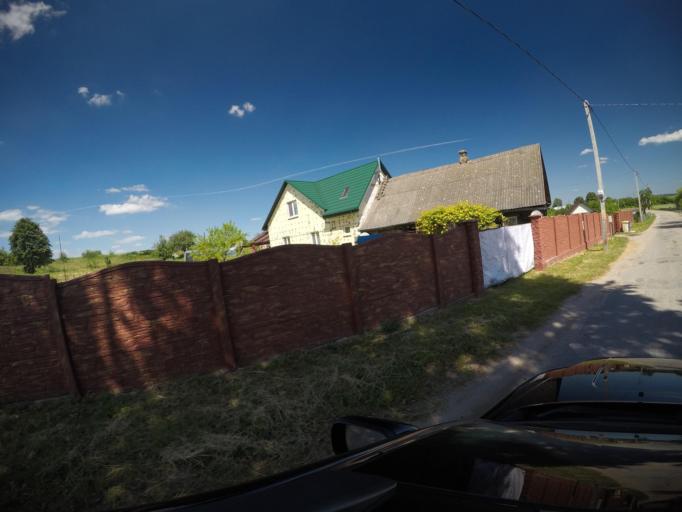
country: BY
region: Grodnenskaya
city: Hrodna
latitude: 53.7278
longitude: 23.8503
